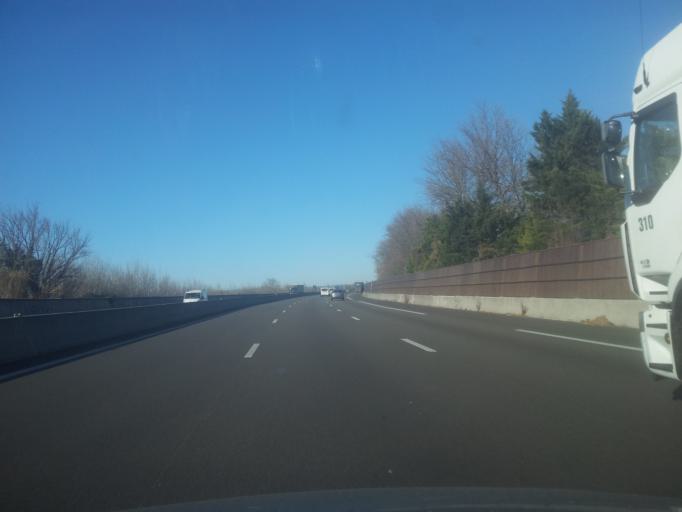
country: FR
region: Provence-Alpes-Cote d'Azur
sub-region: Departement du Vaucluse
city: Mornas
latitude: 44.2006
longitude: 4.7266
